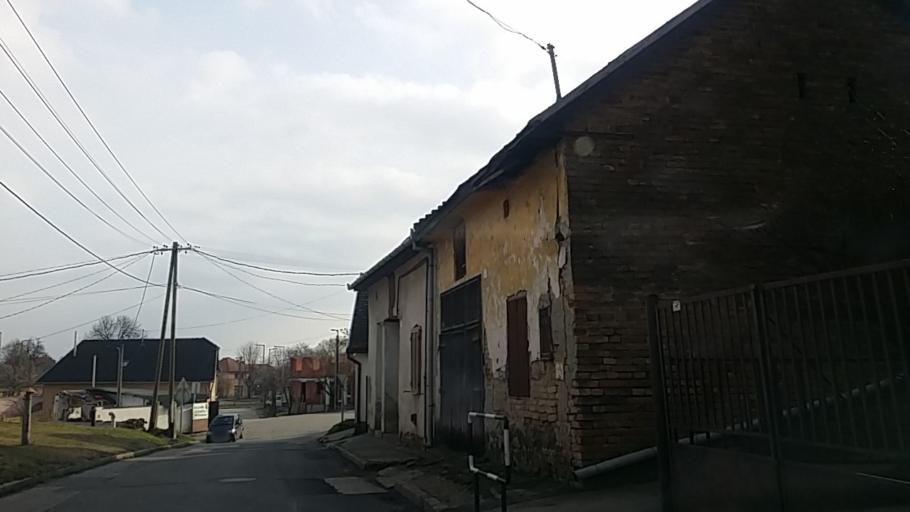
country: HU
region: Tolna
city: Szekszard
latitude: 46.3621
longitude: 18.7028
